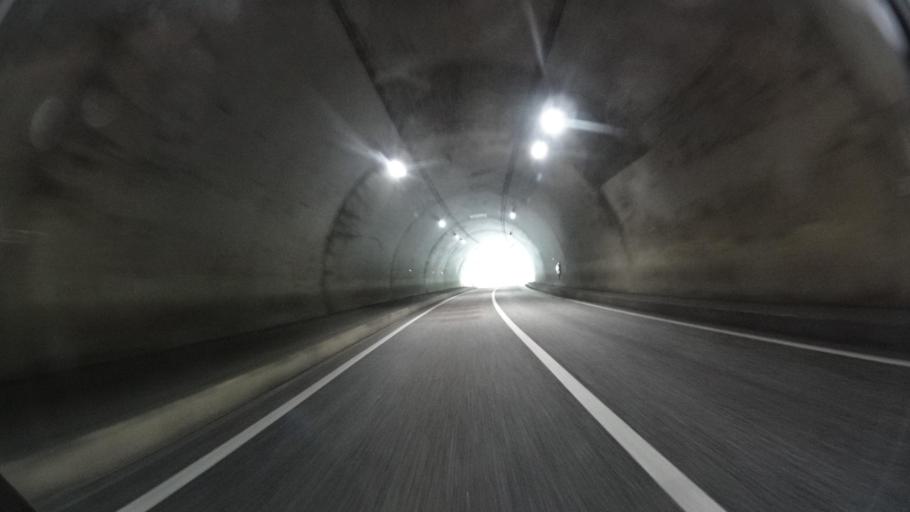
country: JP
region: Kyoto
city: Maizuru
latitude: 35.5217
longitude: 135.3533
